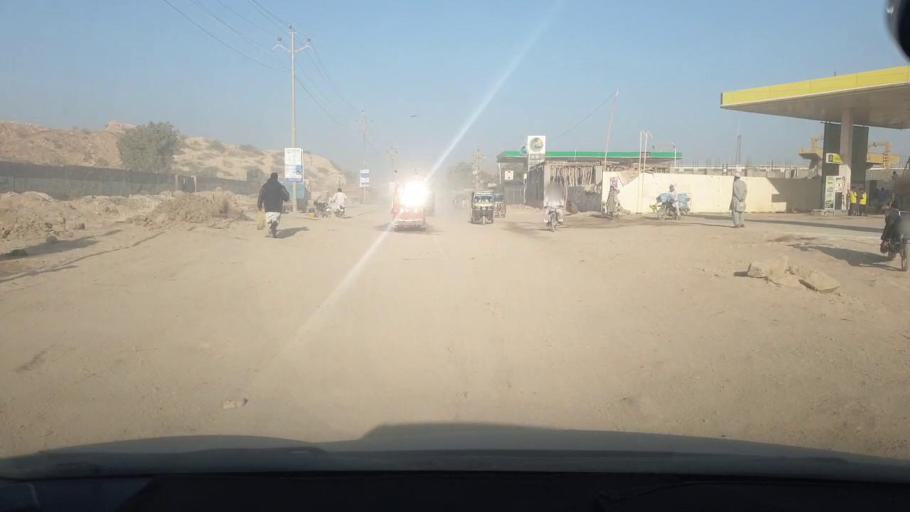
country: PK
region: Sindh
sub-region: Karachi District
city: Karachi
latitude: 24.9755
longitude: 67.0400
